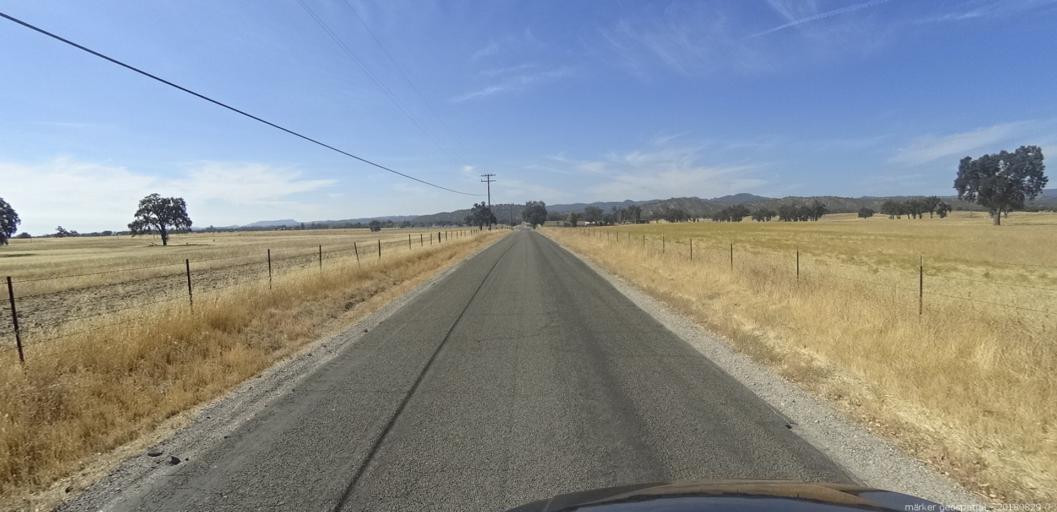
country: US
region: California
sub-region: Monterey County
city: King City
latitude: 35.9403
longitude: -121.0821
